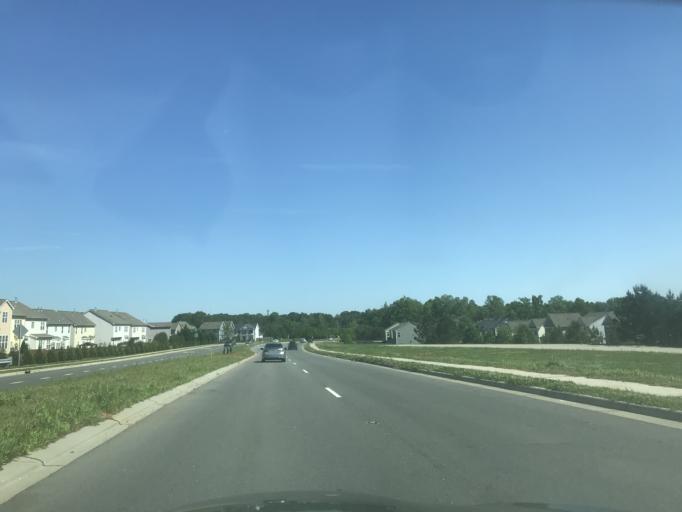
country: US
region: North Carolina
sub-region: Wake County
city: Raleigh
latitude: 35.7362
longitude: -78.6622
